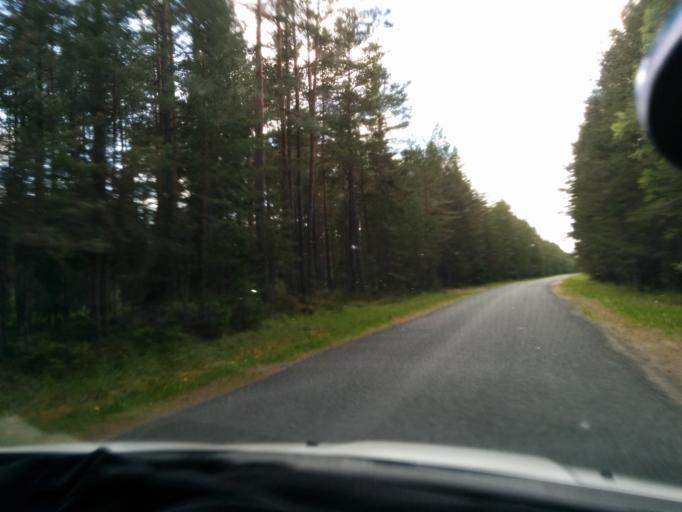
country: EE
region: Harju
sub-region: Loksa linn
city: Loksa
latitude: 59.5675
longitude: 25.7004
